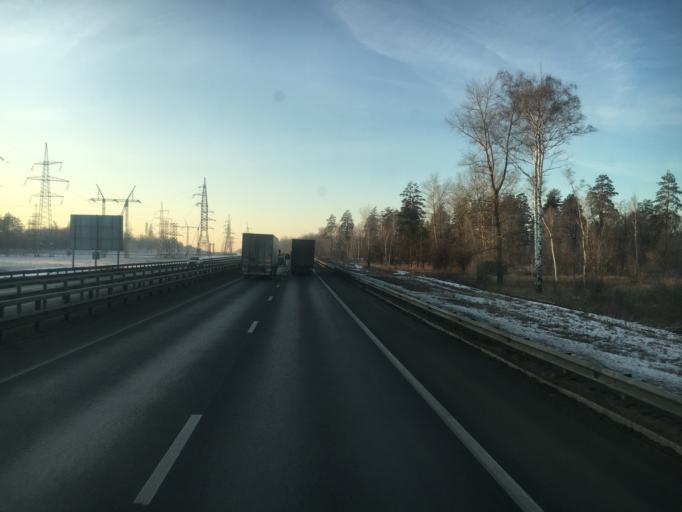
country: RU
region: Samara
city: Pribrezhnyy
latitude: 53.5183
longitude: 49.8257
